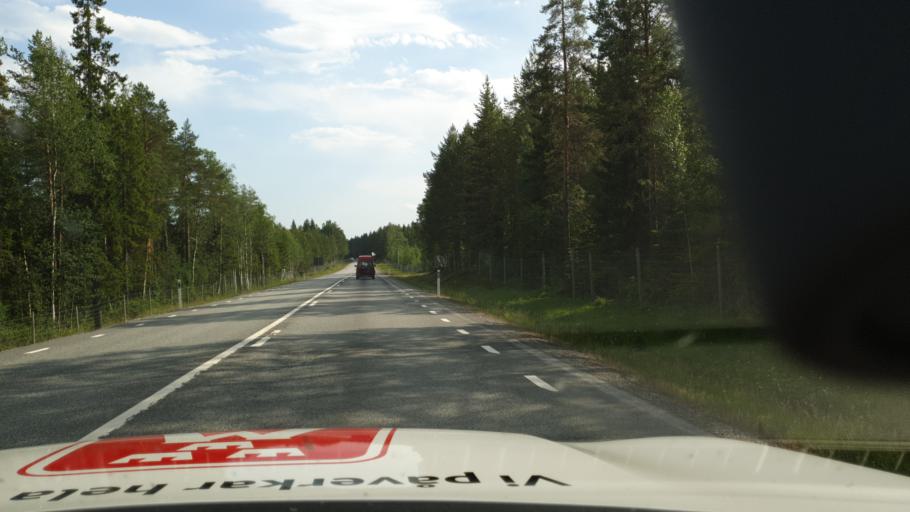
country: SE
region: Vaesterbotten
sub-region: Skelleftea Kommun
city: Burea
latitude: 64.5336
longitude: 21.2586
